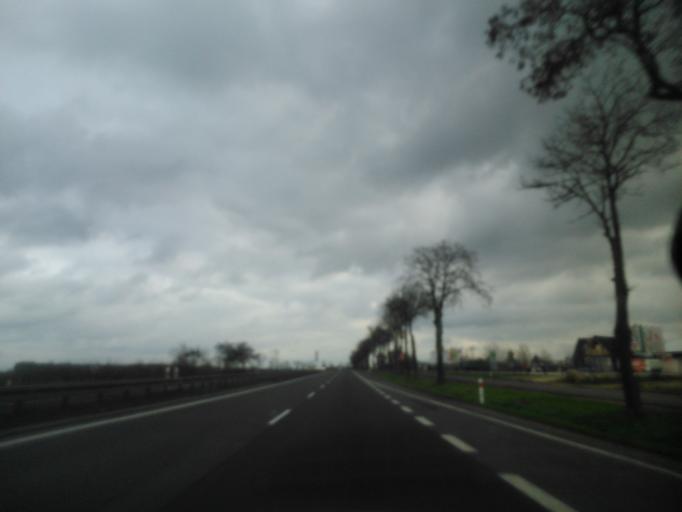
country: PL
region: Masovian Voivodeship
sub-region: Powiat plonski
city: Plonsk
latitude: 52.5947
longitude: 20.4342
